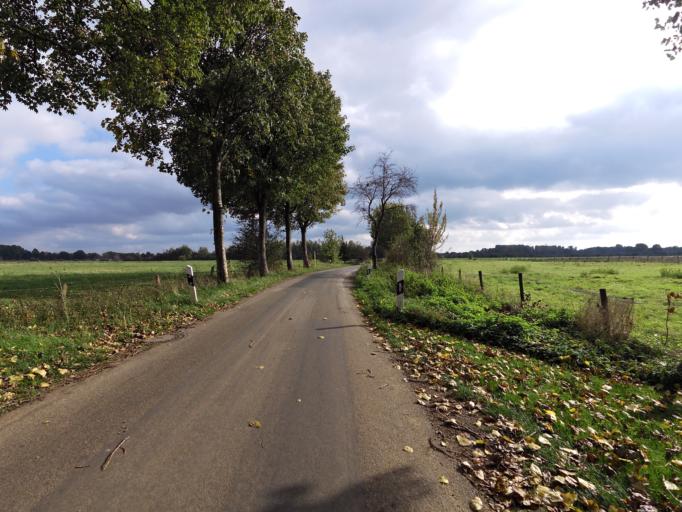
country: DE
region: North Rhine-Westphalia
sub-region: Regierungsbezirk Munster
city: Isselburg
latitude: 51.8245
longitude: 6.4794
